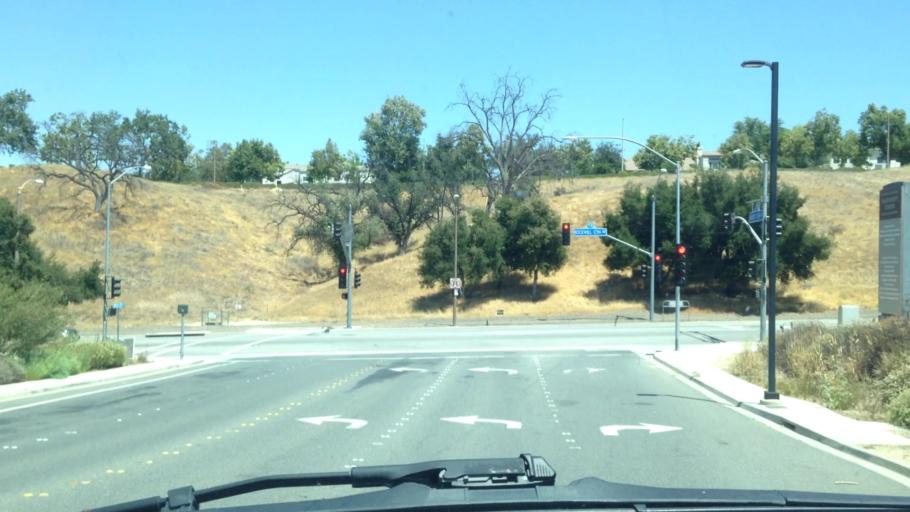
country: US
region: California
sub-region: Los Angeles County
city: Santa Clarita
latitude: 34.4010
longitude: -118.5674
